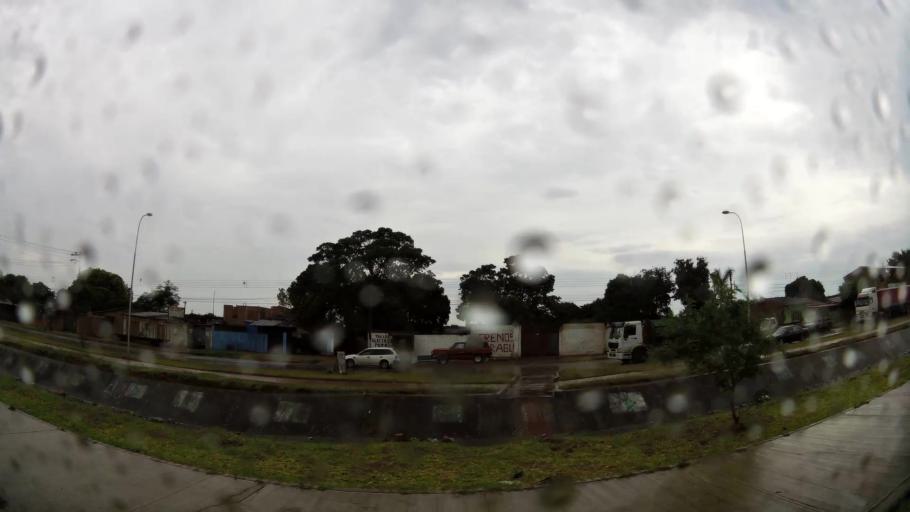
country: BO
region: Santa Cruz
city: Santa Cruz de la Sierra
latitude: -17.8120
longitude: -63.1355
